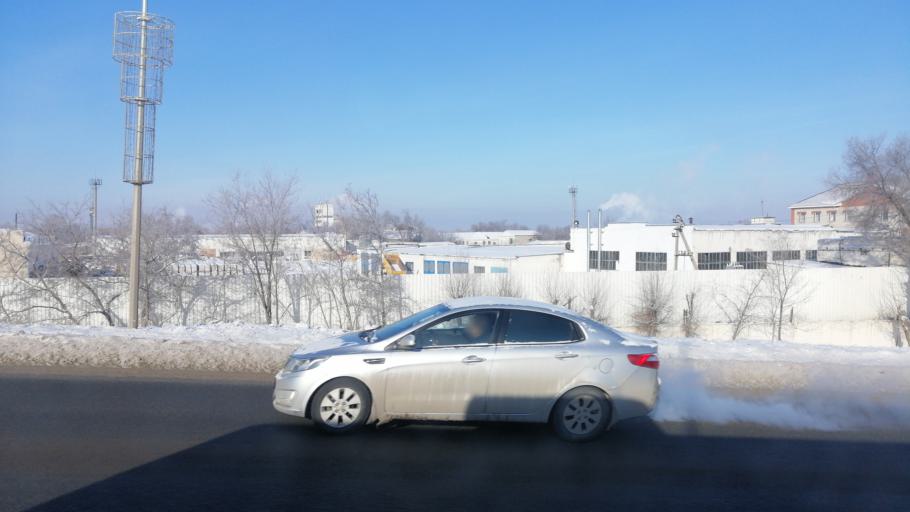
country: KZ
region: Aqtoebe
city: Aqtobe
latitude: 50.2958
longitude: 57.1817
